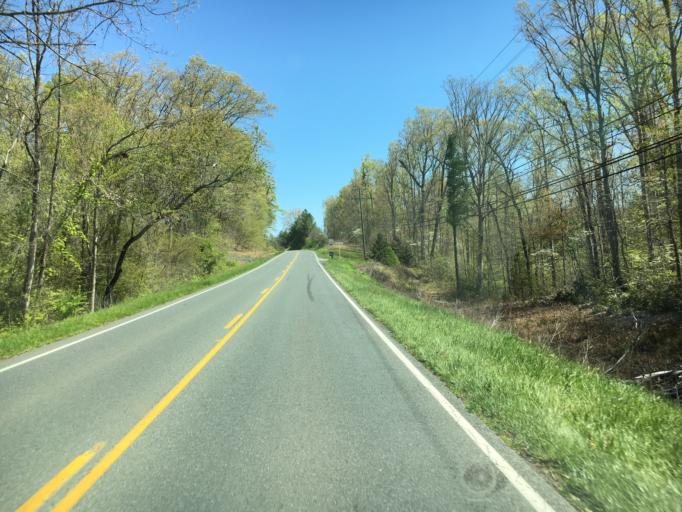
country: US
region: Virginia
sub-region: Augusta County
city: Crimora
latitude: 38.1441
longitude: -78.8422
